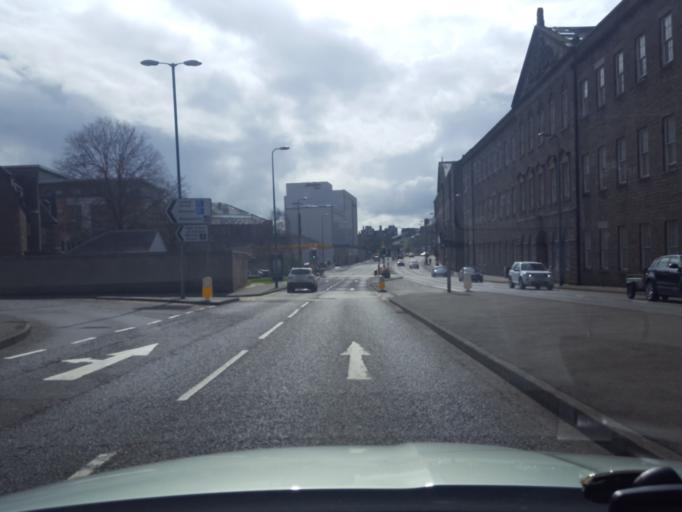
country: GB
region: Scotland
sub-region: Dundee City
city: Dundee
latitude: 56.4621
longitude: -2.9786
